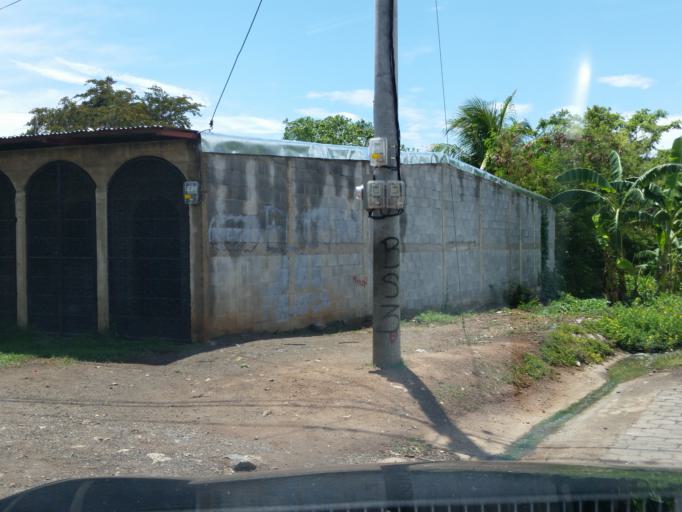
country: NI
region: Granada
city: Granada
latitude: 11.9254
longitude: -85.9504
